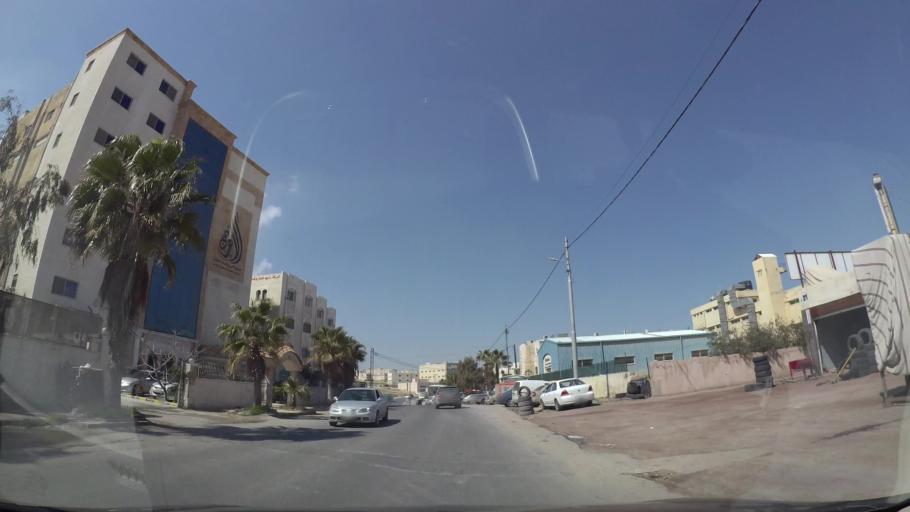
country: JO
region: Zarqa
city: Russeifa
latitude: 31.9898
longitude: 36.0150
